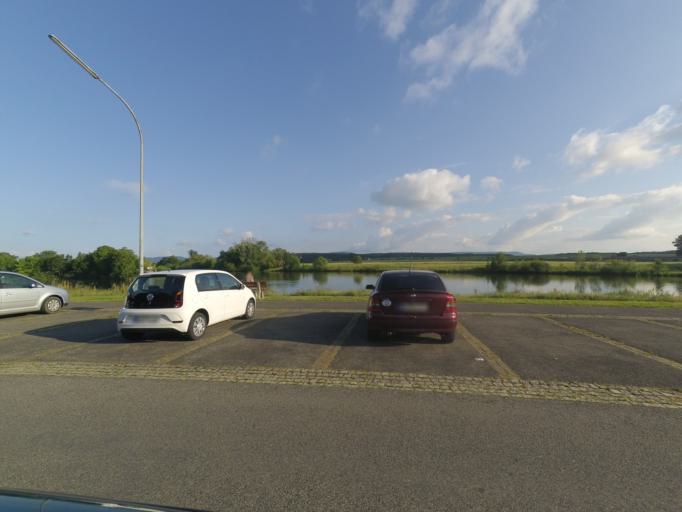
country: DE
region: Bavaria
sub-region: Regierungsbezirk Unterfranken
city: Hassfurt
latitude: 50.0297
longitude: 10.5107
